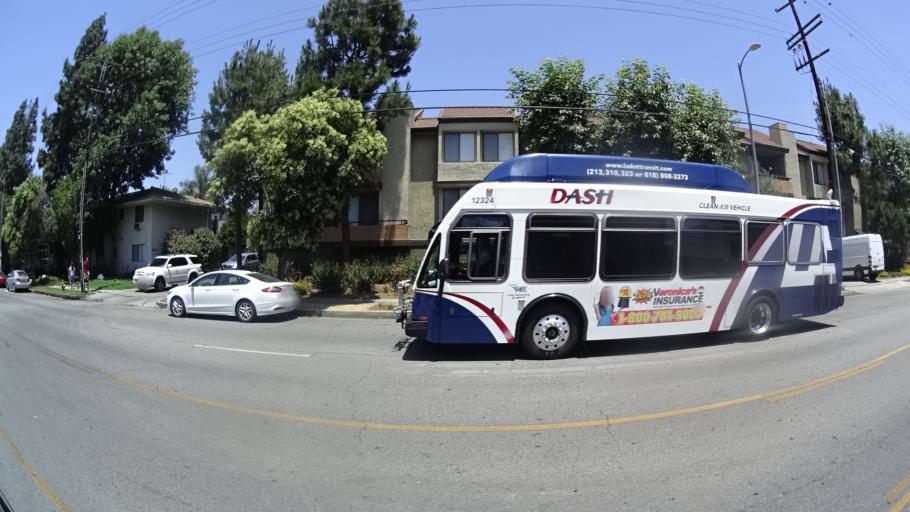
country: US
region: California
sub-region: Los Angeles County
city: Van Nuys
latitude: 34.2084
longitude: -118.4602
